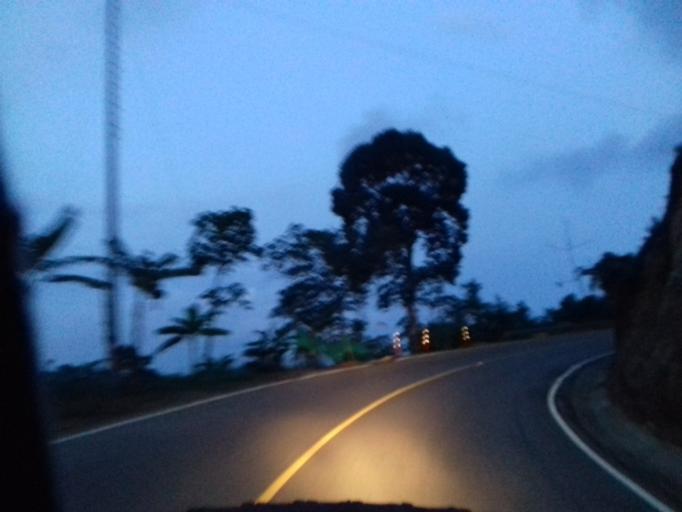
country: CO
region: Tolima
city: Libano
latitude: 4.9598
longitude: -74.9834
